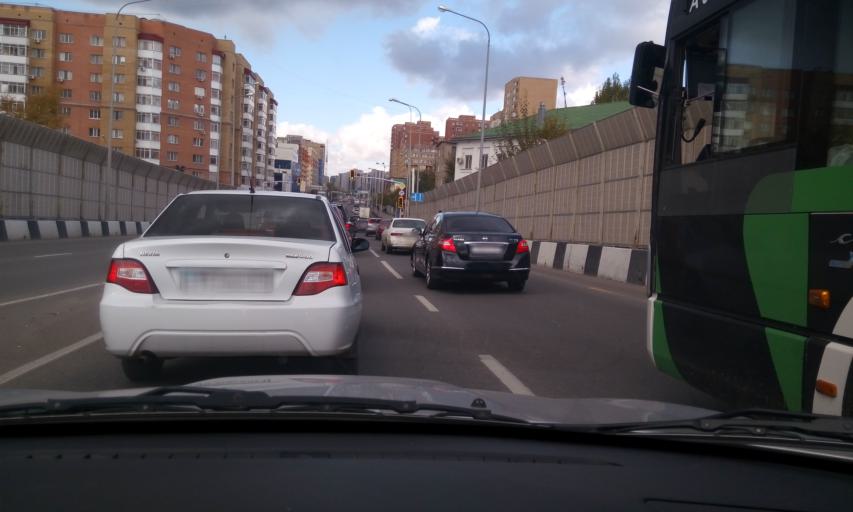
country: KZ
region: Astana Qalasy
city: Astana
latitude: 51.1595
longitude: 71.4636
